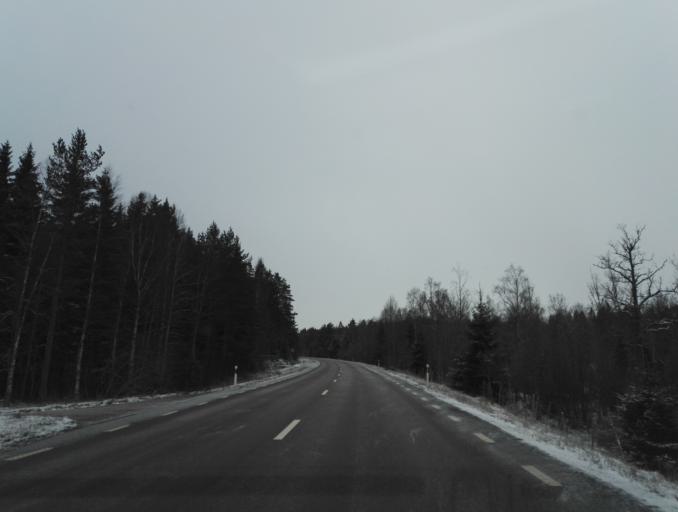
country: SE
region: Kronoberg
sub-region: Uppvidinge Kommun
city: Aseda
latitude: 57.1783
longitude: 15.4964
